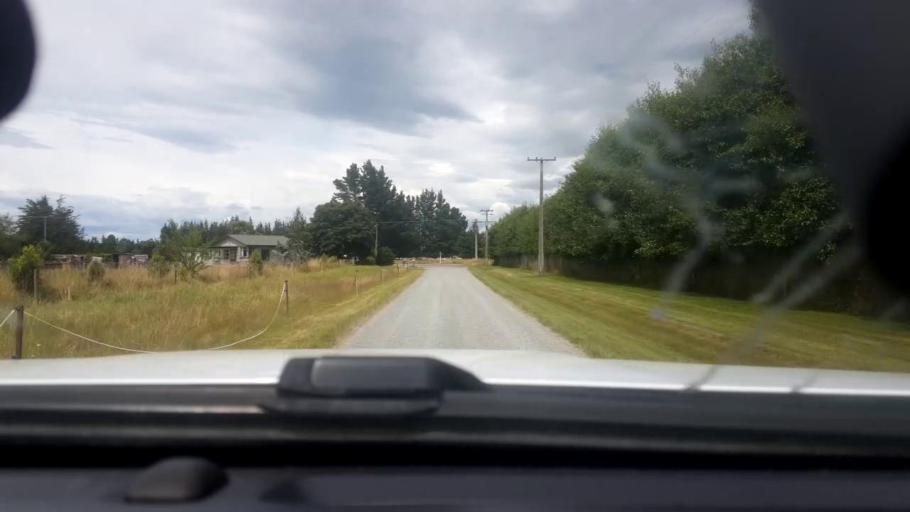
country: NZ
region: Canterbury
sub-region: Timaru District
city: Pleasant Point
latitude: -44.1436
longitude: 171.2888
